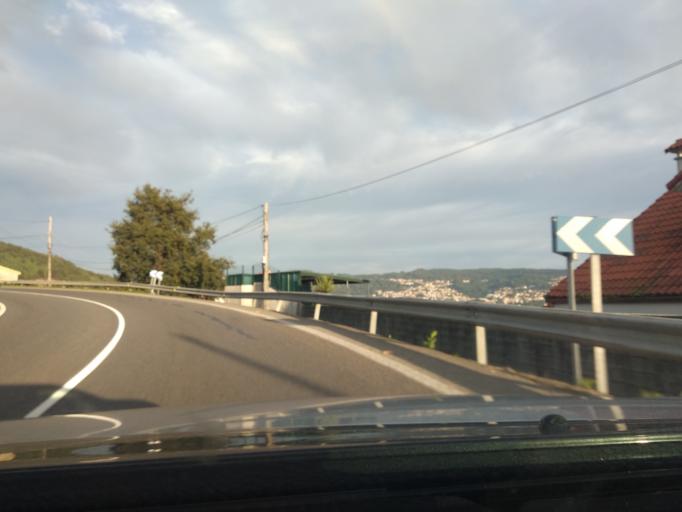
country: ES
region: Galicia
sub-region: Provincia de Pontevedra
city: Moana
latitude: 42.2805
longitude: -8.7104
